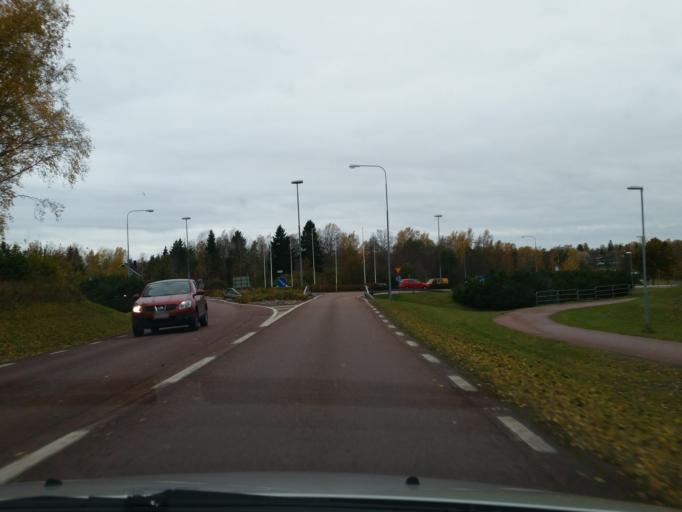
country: AX
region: Mariehamns stad
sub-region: Mariehamn
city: Mariehamn
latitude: 60.1138
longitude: 19.9314
